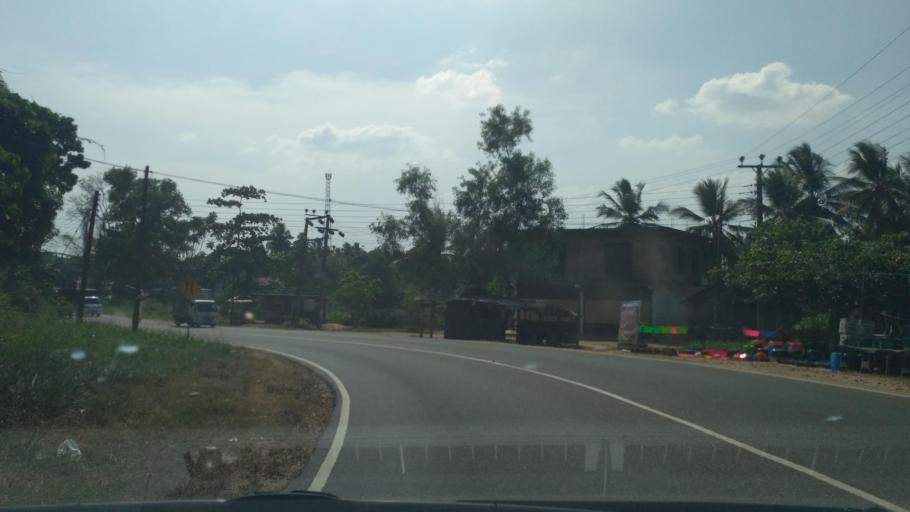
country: LK
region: North Western
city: Kuliyapitiya
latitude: 7.3324
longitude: 80.0279
